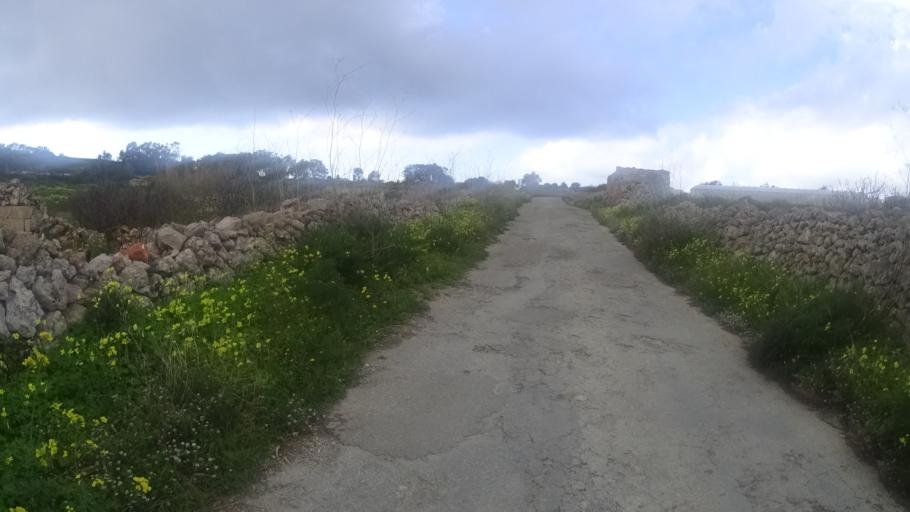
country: MT
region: L-Imgarr
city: Imgarr
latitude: 35.8961
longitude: 14.3671
